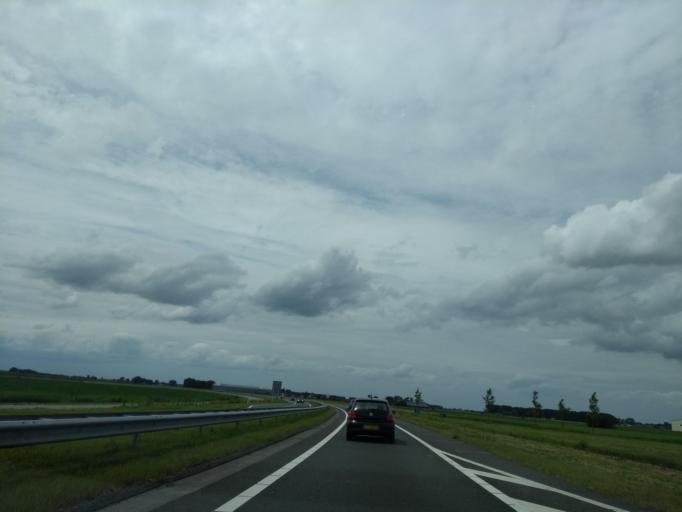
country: NL
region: Zeeland
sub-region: Gemeente Borsele
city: Borssele
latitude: 51.3250
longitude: 3.6794
